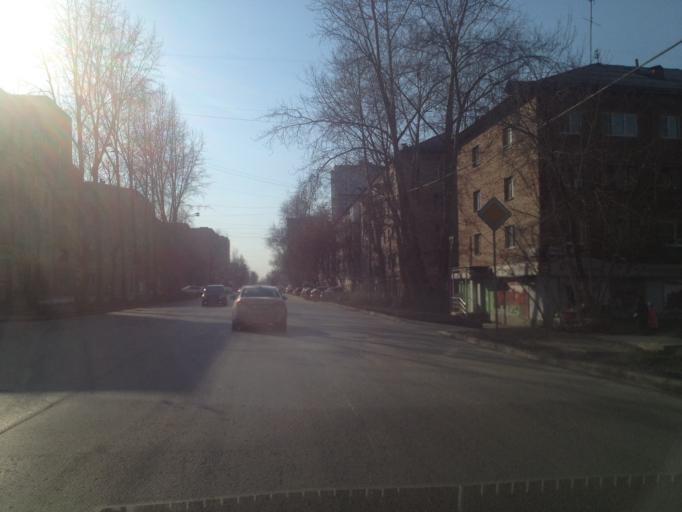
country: RU
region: Sverdlovsk
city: Yekaterinburg
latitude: 56.8615
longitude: 60.6427
